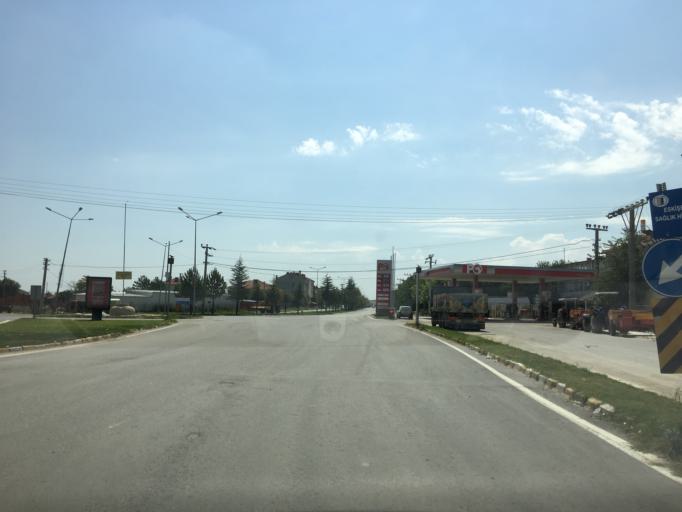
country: TR
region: Eskisehir
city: Cifteler
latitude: 39.3695
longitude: 31.0354
